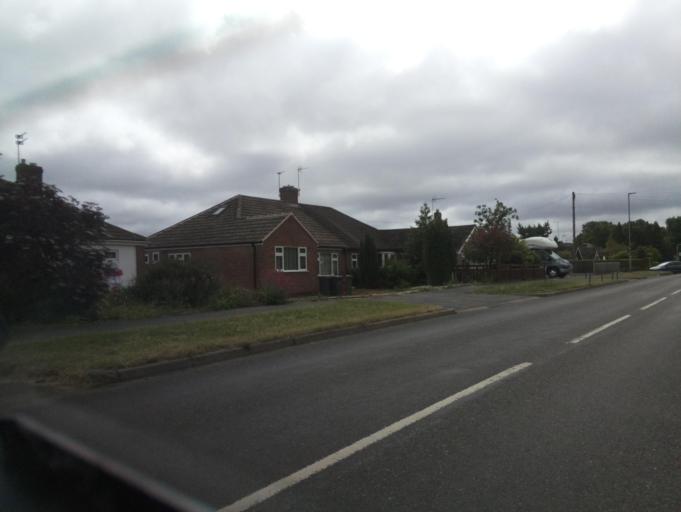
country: GB
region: England
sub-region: Leicestershire
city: Coalville
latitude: 52.7295
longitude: -1.3434
